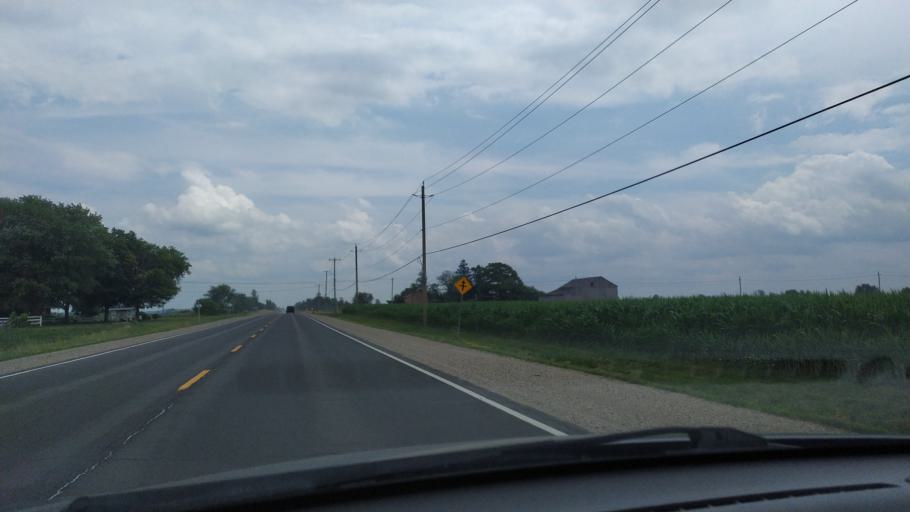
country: CA
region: Ontario
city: Stratford
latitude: 43.3701
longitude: -80.8900
